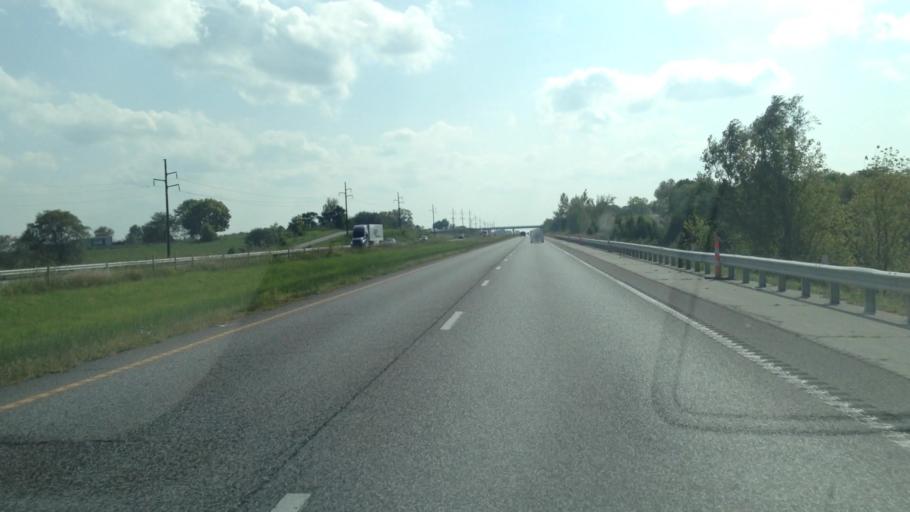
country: US
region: Missouri
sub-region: Clay County
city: Kearney
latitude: 39.3312
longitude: -94.3922
